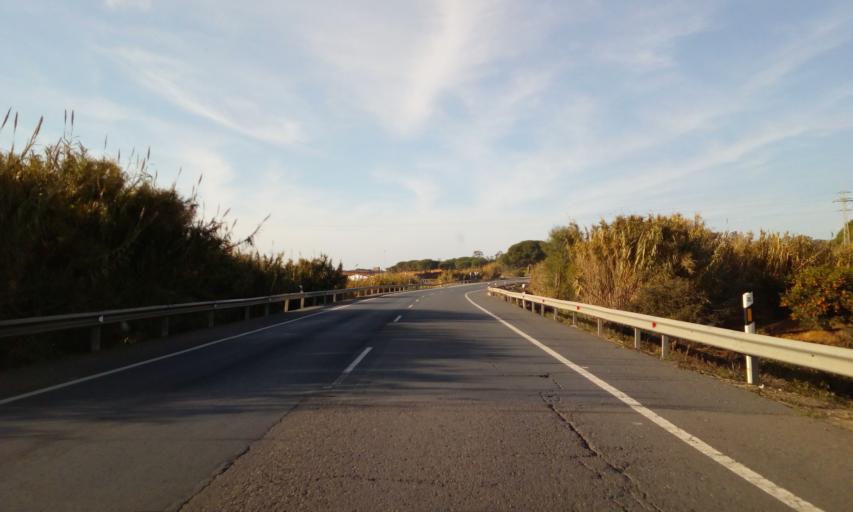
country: ES
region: Andalusia
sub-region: Provincia de Huelva
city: Isla Cristina
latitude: 37.2460
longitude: -7.2705
